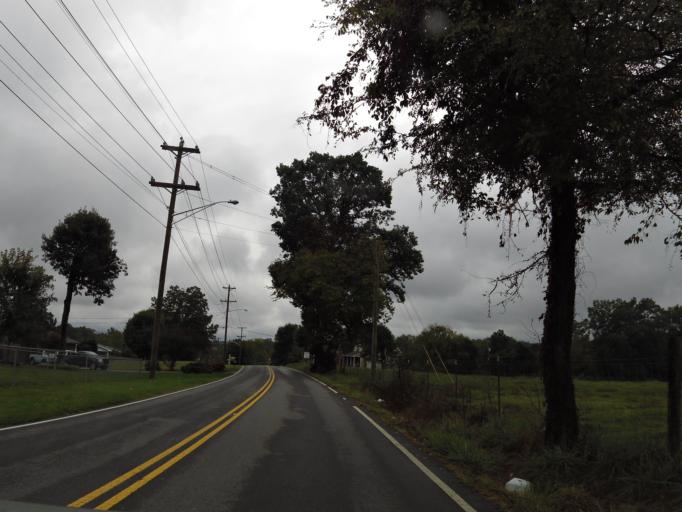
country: US
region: Tennessee
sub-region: Bradley County
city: Hopewell
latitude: 35.2120
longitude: -84.8999
